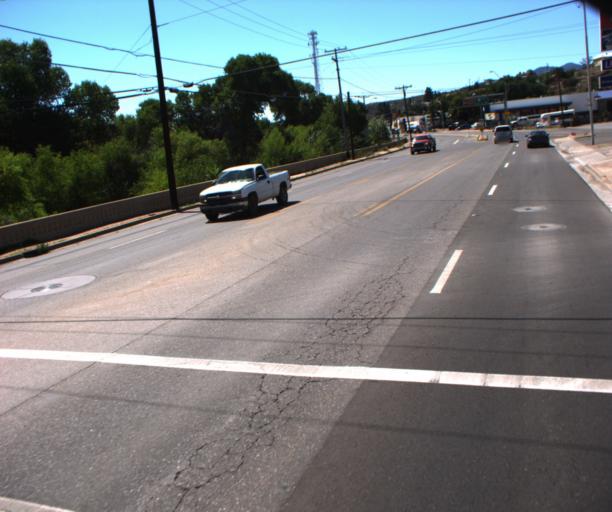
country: US
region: Arizona
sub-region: Gila County
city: Globe
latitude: 33.4033
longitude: -110.7927
